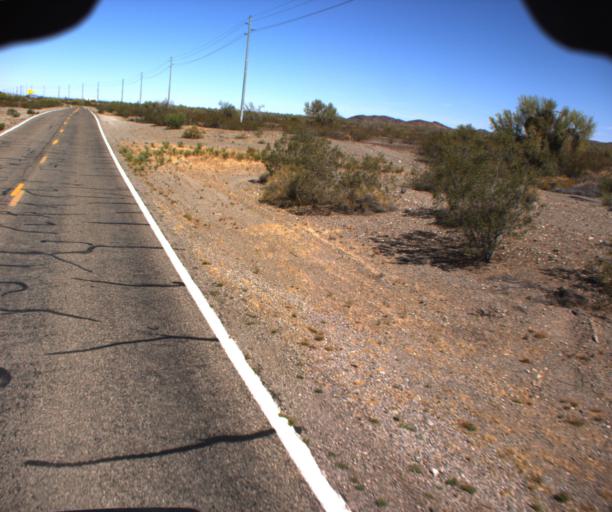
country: US
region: Arizona
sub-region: La Paz County
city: Salome
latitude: 33.7404
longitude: -113.7412
